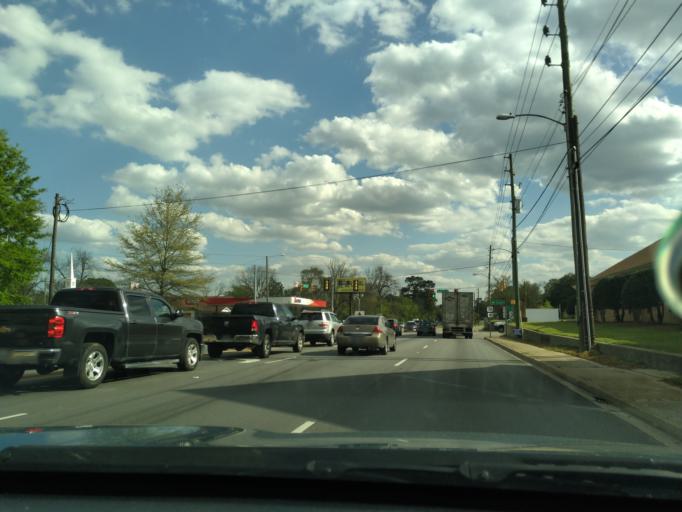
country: US
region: South Carolina
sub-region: Florence County
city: Florence
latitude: 34.1947
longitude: -79.7619
